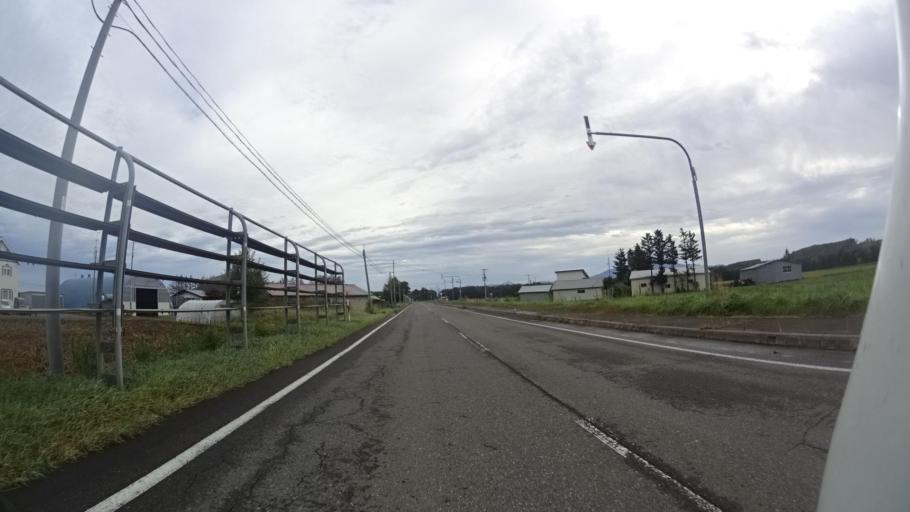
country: JP
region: Hokkaido
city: Abashiri
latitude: 43.8577
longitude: 144.6104
